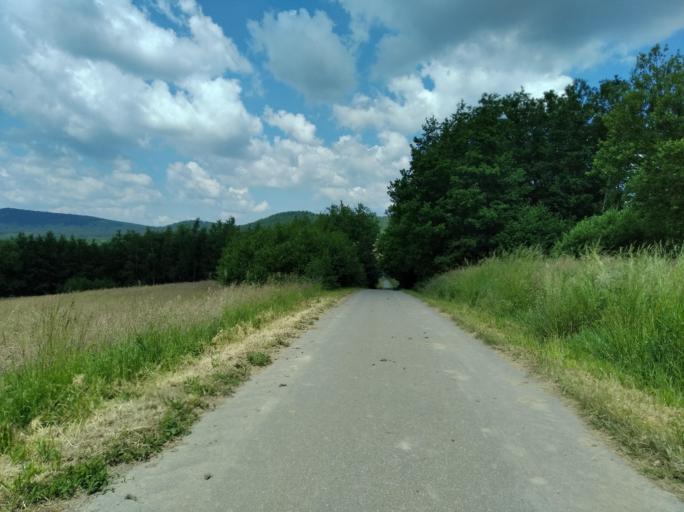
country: PL
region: Subcarpathian Voivodeship
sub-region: Powiat strzyzowski
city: Jawornik
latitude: 49.7834
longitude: 21.8674
